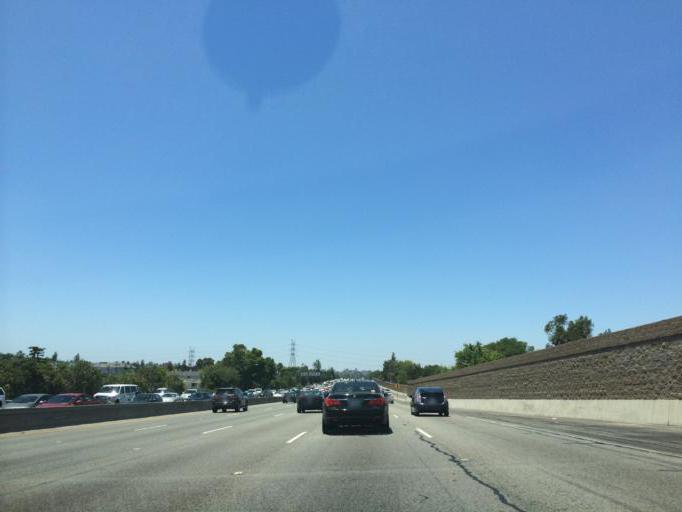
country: US
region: California
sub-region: Los Angeles County
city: Northridge
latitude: 34.1734
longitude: -118.5364
